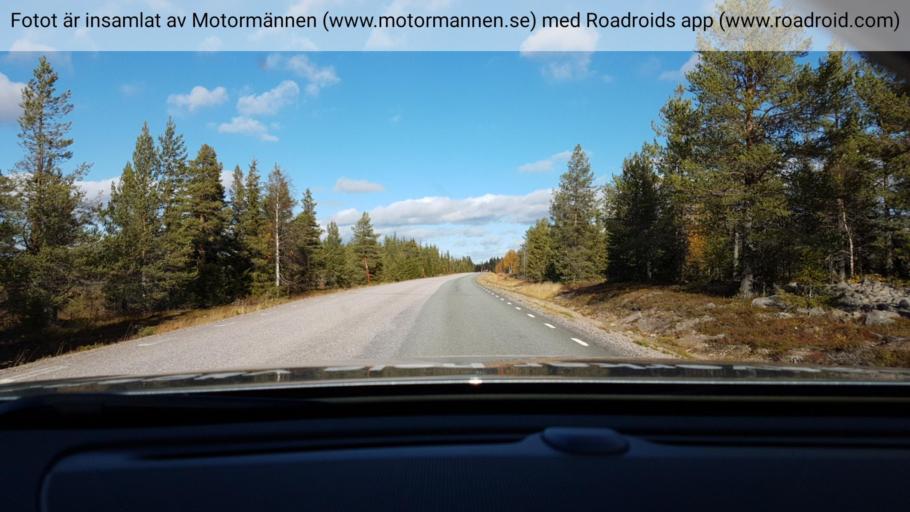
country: SE
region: Norrbotten
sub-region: Arjeplogs Kommun
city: Arjeplog
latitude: 65.8717
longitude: 18.4087
